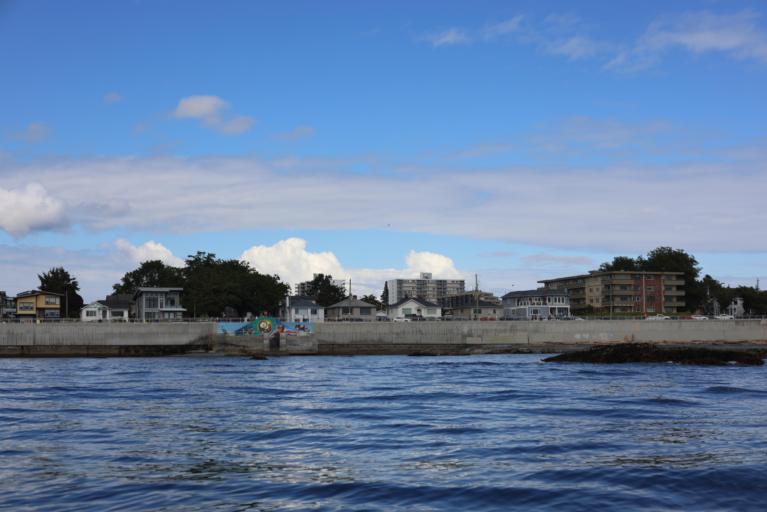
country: CA
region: British Columbia
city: Victoria
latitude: 48.4123
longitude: -123.3836
